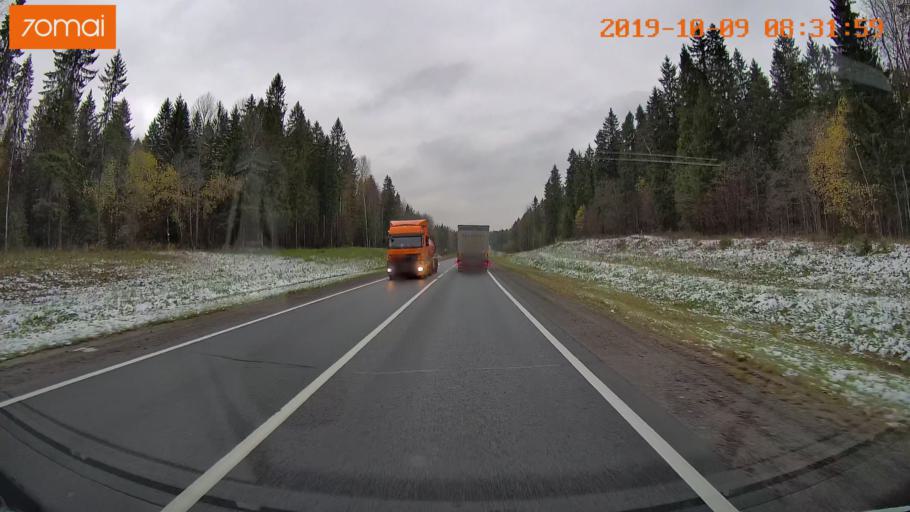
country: RU
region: Vologda
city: Gryazovets
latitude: 58.8608
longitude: 40.1989
